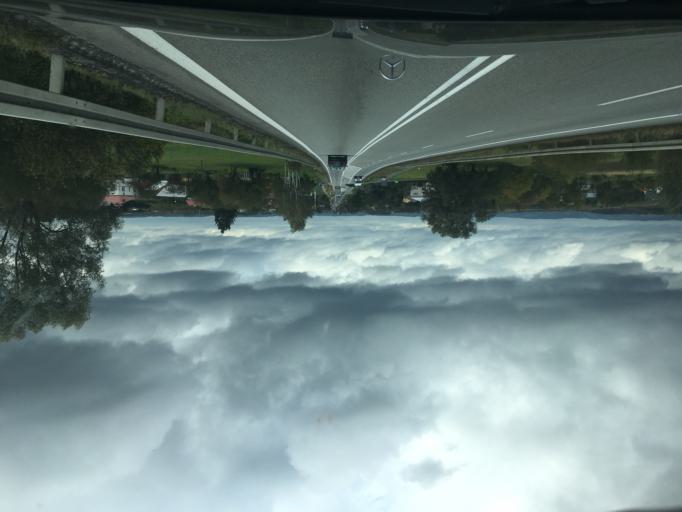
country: PL
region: Subcarpathian Voivodeship
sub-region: Powiat krosnienski
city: Miejsce Piastowe
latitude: 49.6130
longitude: 21.7478
